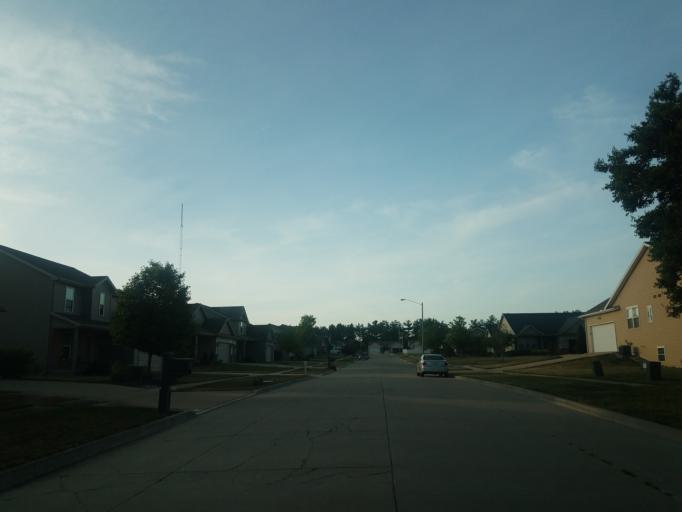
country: US
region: Illinois
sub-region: McLean County
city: Bloomington
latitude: 40.4469
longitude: -89.0098
